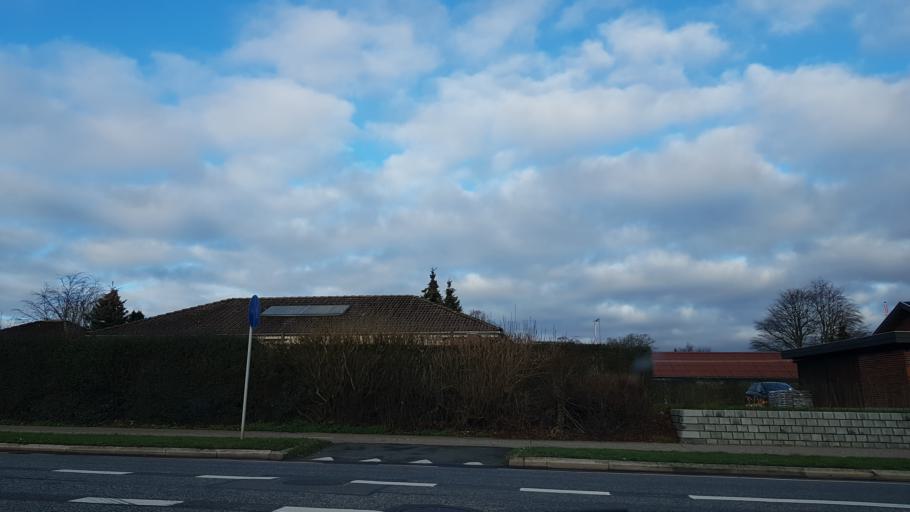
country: DK
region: Zealand
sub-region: Slagelse Kommune
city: Slagelse
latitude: 55.3896
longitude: 11.3294
